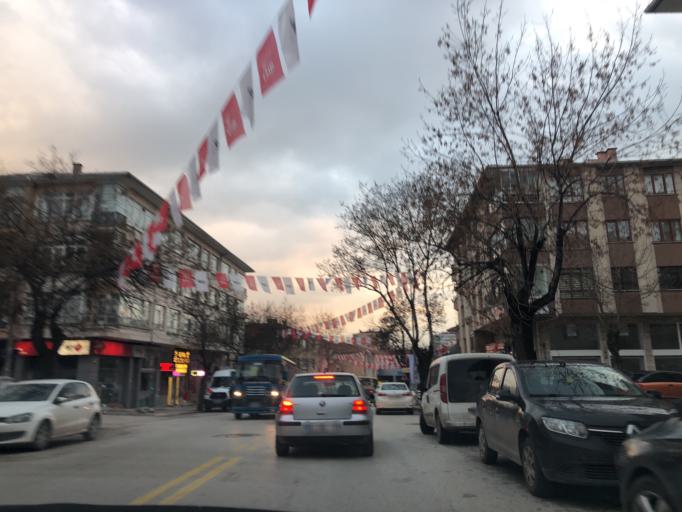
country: TR
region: Ankara
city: Ankara
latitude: 39.9644
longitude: 32.8087
